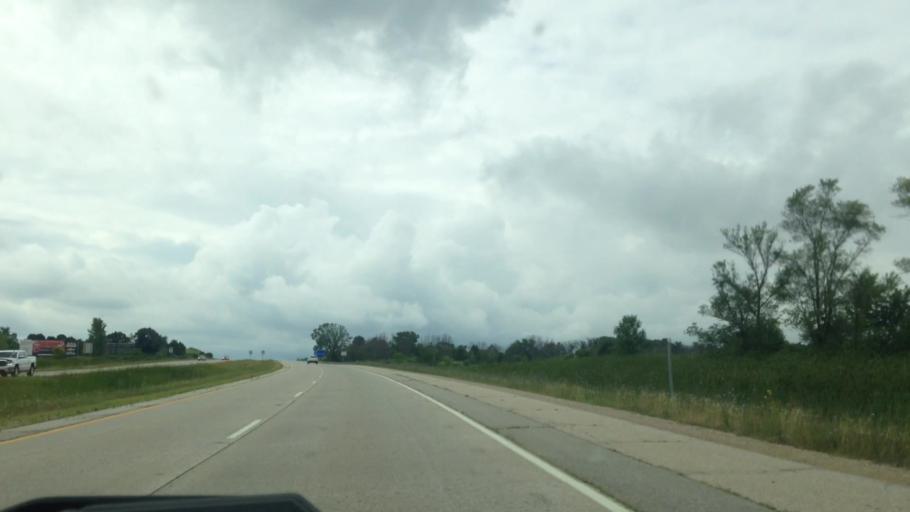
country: US
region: Wisconsin
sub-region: Washington County
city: Jackson
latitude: 43.2953
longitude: -88.1874
